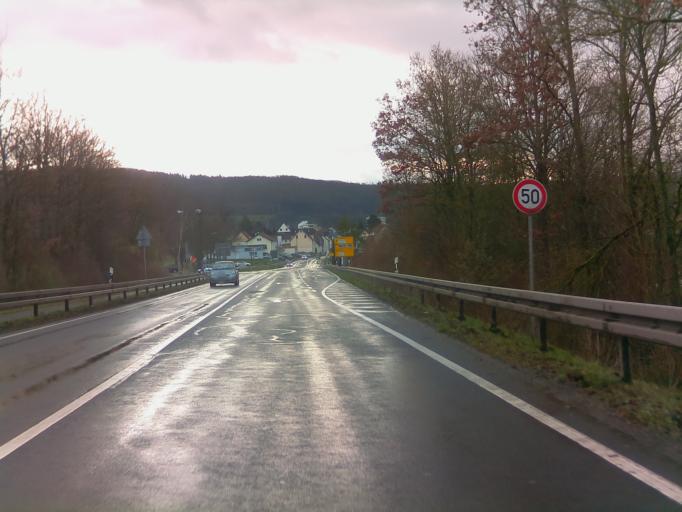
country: DE
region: Hesse
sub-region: Regierungsbezirk Darmstadt
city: Schluchtern
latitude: 50.3588
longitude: 9.5244
